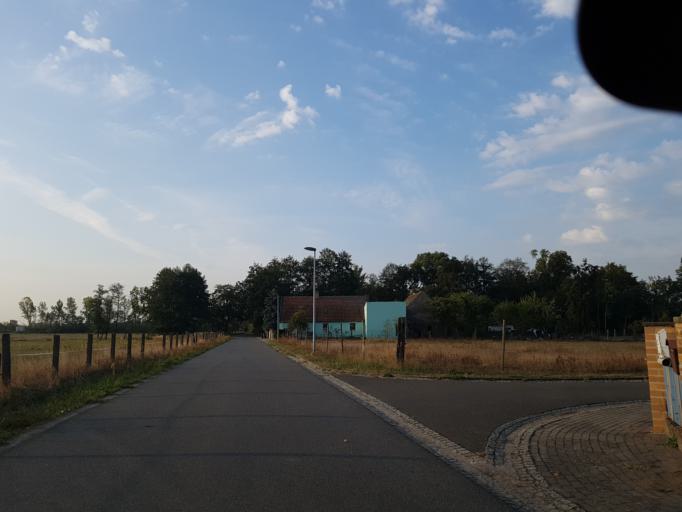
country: DE
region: Brandenburg
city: Hohenleipisch
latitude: 51.4644
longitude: 13.5665
